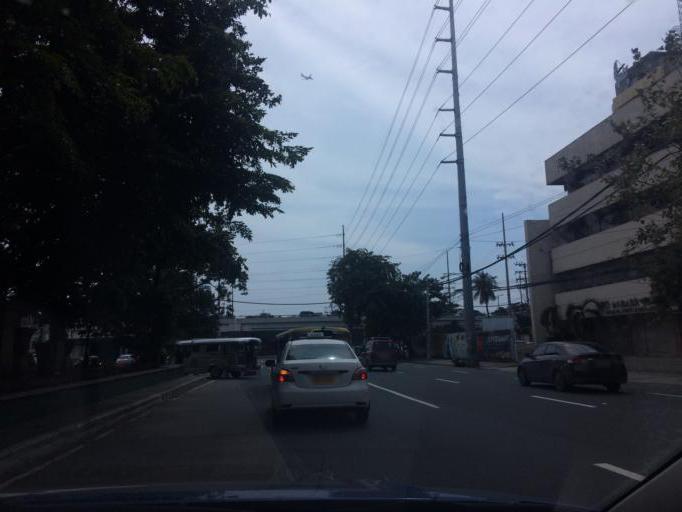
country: PH
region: Metro Manila
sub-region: City of Manila
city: Port Area
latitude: 14.5527
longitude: 120.9906
